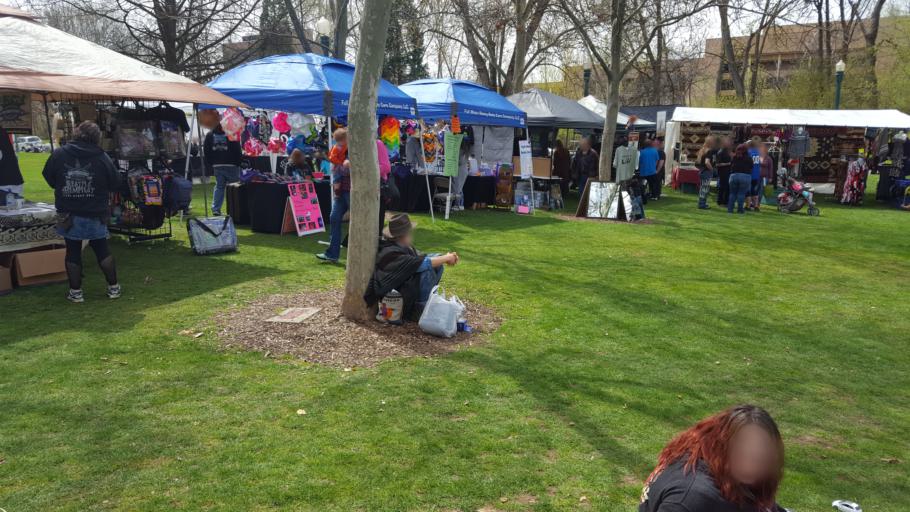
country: US
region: Idaho
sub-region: Ada County
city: Boise
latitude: 43.6083
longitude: -116.2064
